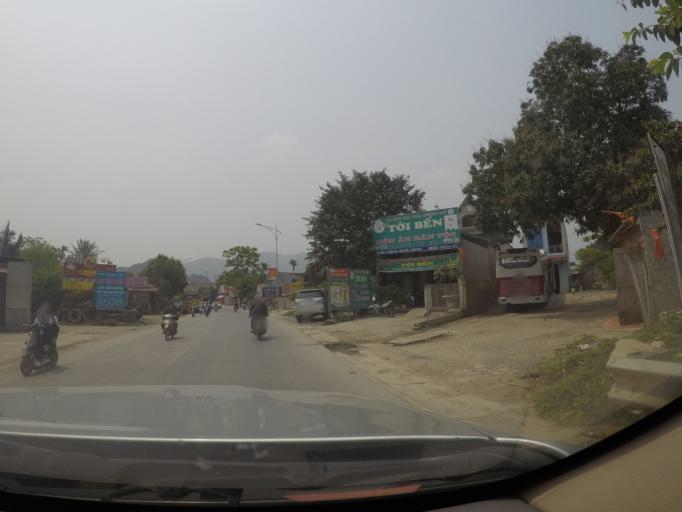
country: VN
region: Thanh Hoa
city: Thi Tran Cam Thuy
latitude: 20.2104
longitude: 105.4772
